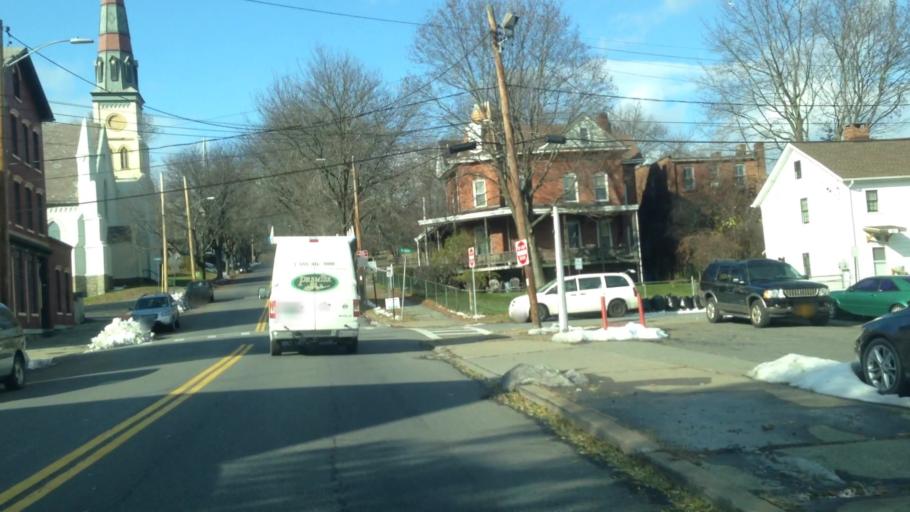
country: US
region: New York
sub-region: Ulster County
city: Kingston
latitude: 41.9177
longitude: -73.9854
